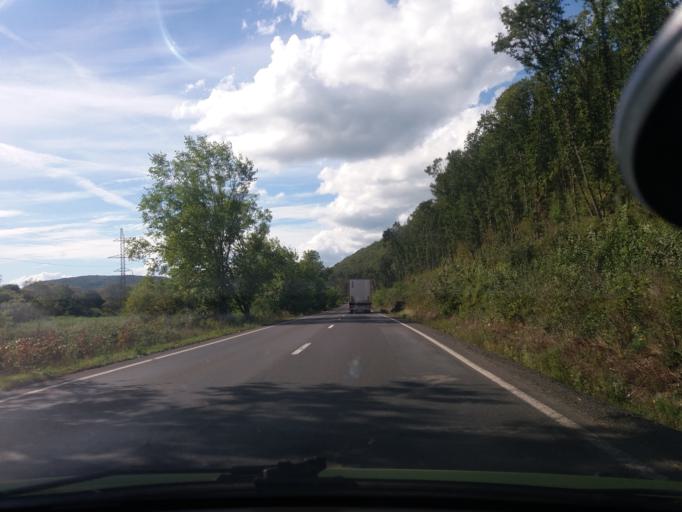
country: RO
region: Hunedoara
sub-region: Comuna Zam
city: Zam
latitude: 46.0147
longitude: 22.4243
